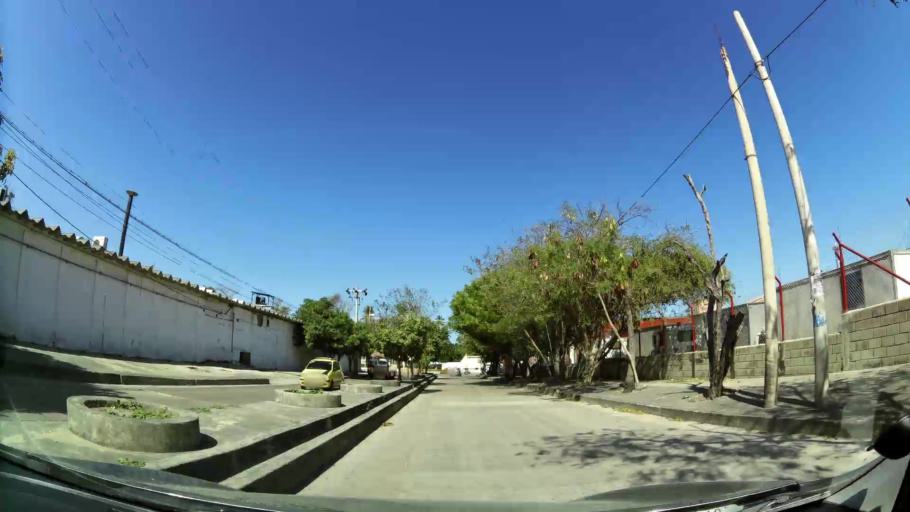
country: CO
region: Atlantico
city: Barranquilla
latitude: 11.0026
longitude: -74.7867
